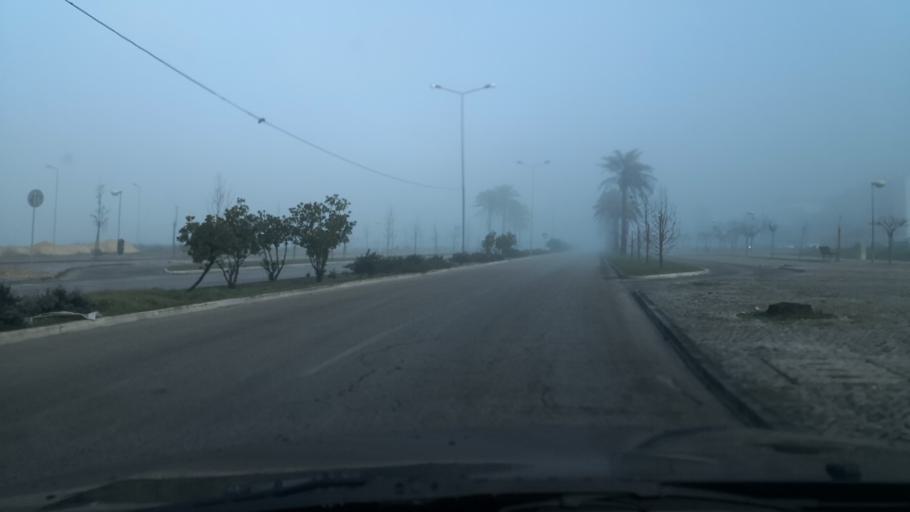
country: PT
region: Setubal
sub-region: Palmela
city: Pinhal Novo
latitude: 38.6240
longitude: -8.9183
